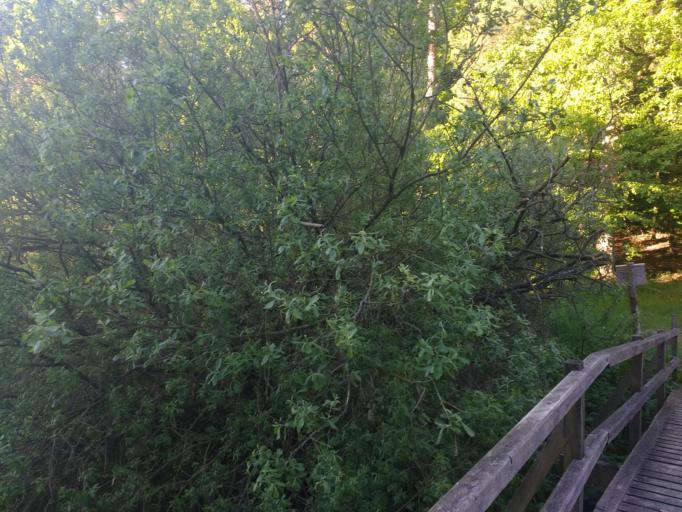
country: DE
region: Mecklenburg-Vorpommern
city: Neukloster
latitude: 53.8426
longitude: 11.7097
